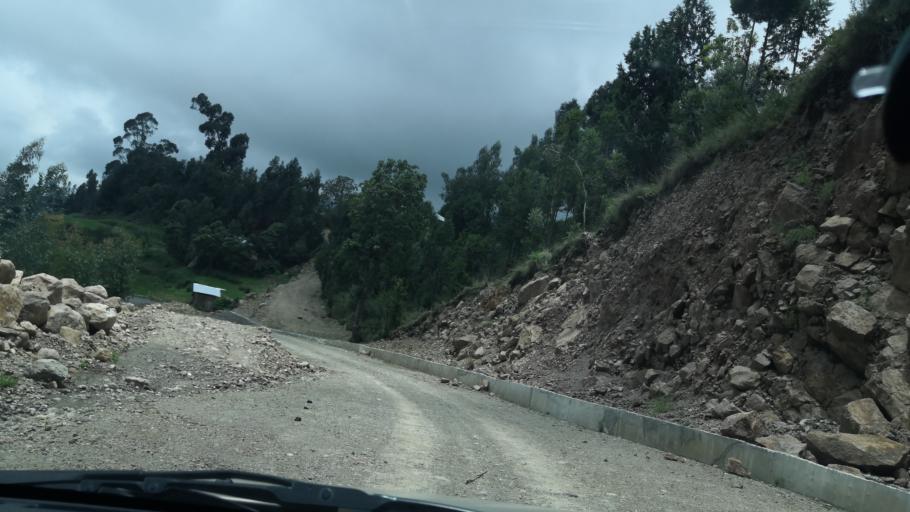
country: ET
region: Amhara
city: Abomsa
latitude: 10.3280
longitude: 39.8394
